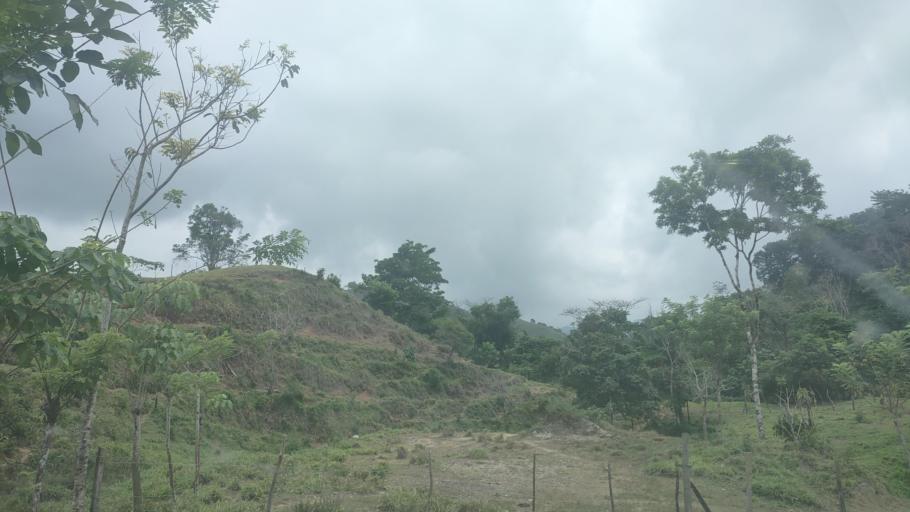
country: MX
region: Tabasco
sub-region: Huimanguillo
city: Francisco Rueda
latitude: 17.4432
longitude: -94.0265
